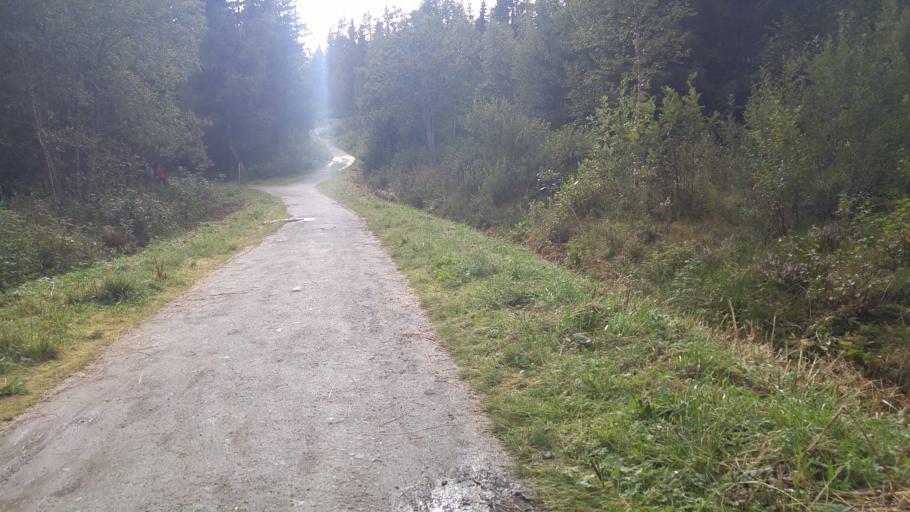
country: NO
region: Sor-Trondelag
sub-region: Trondheim
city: Trondheim
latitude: 63.4082
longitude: 10.3311
